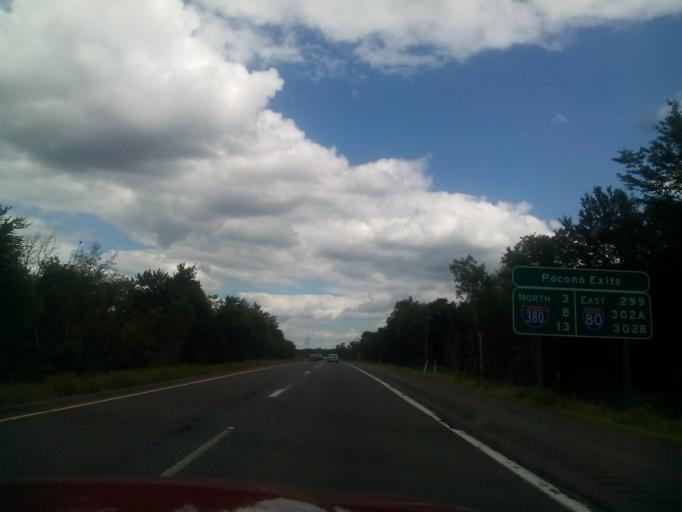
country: US
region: Pennsylvania
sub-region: Monroe County
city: Emerald Lakes
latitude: 41.0711
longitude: -75.4291
